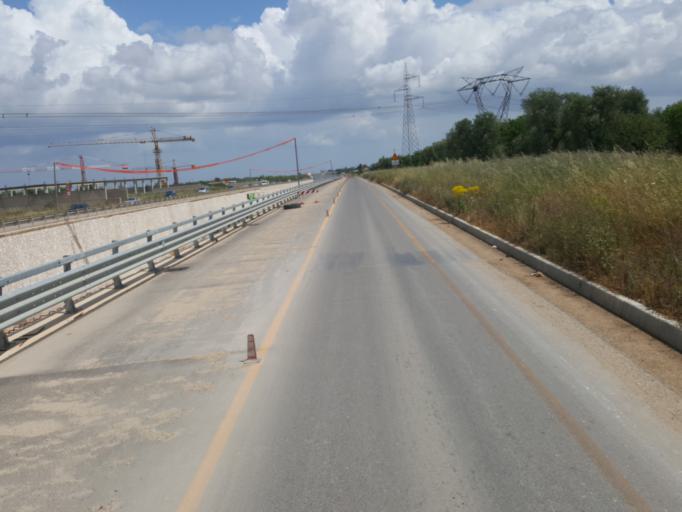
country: IT
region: Apulia
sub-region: Provincia di Bari
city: Bitetto
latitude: 41.0693
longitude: 16.7358
